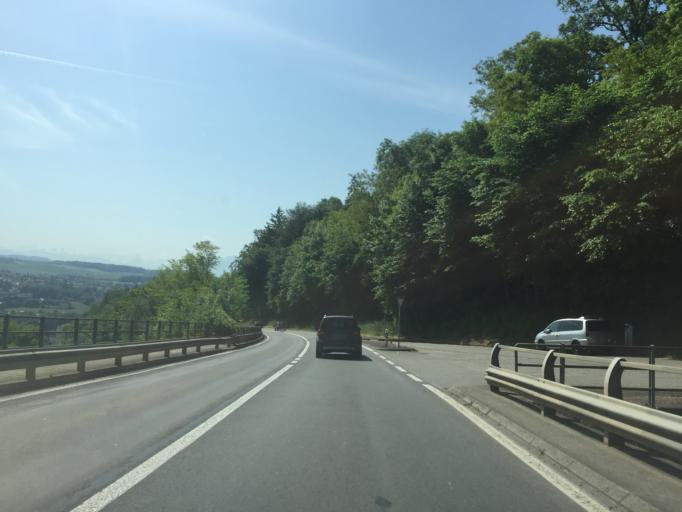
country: CH
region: Vaud
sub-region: Morges District
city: Cossonay
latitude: 46.6104
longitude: 6.5135
